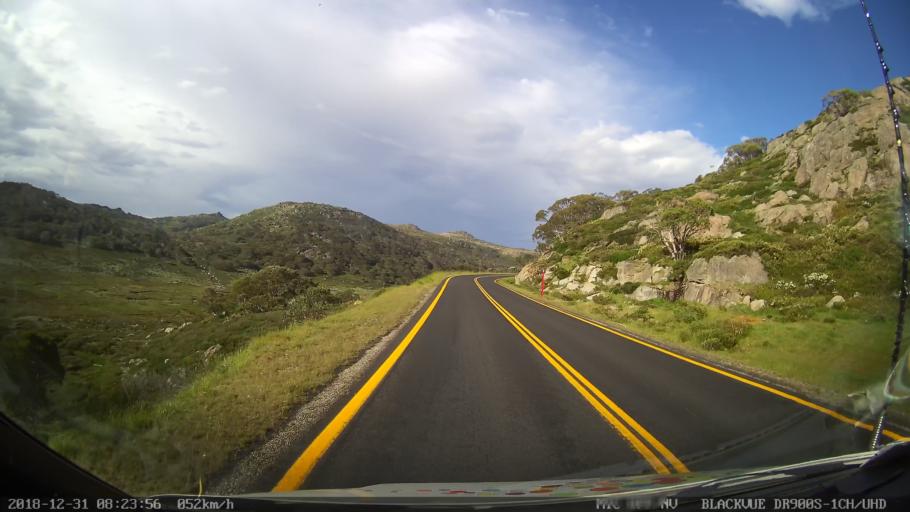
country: AU
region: New South Wales
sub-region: Snowy River
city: Jindabyne
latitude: -36.4295
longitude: 148.3432
